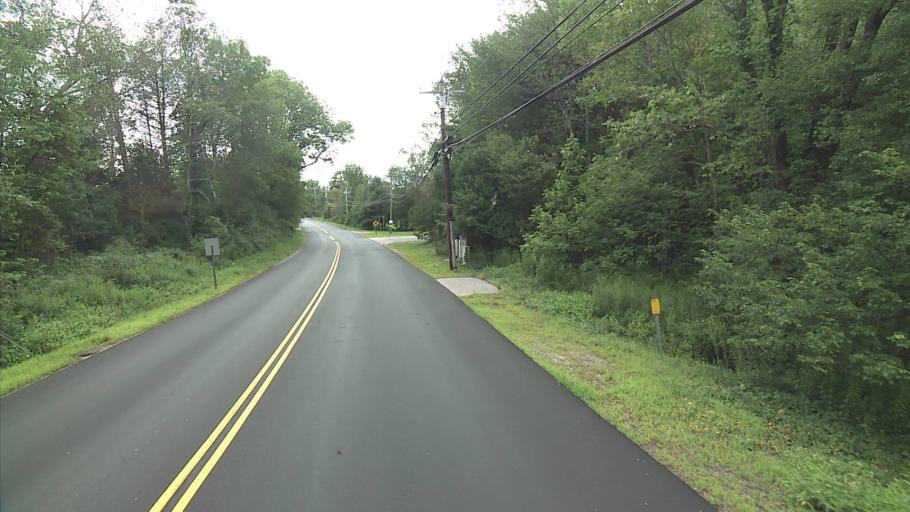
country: US
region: Connecticut
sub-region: Windham County
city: South Woodstock
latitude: 41.9500
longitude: -72.0587
